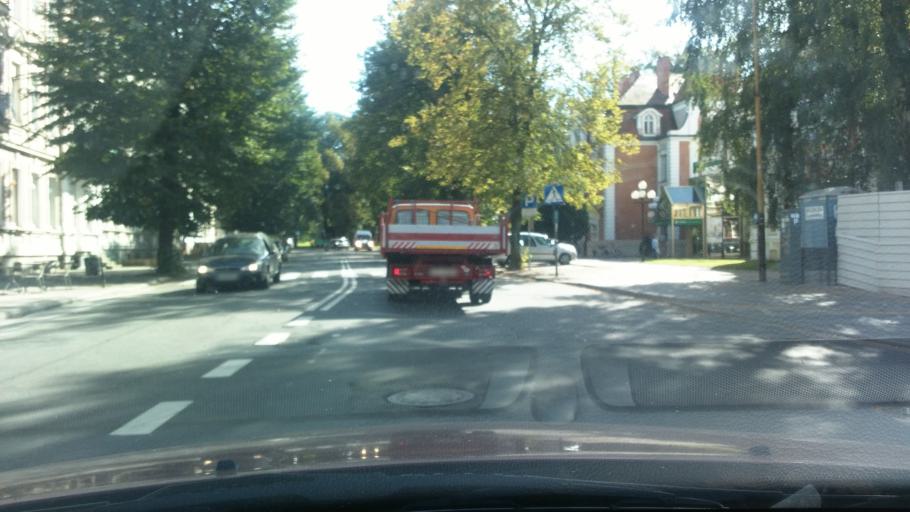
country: PL
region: Lower Silesian Voivodeship
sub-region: Powiat zgorzelecki
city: Zgorzelec
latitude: 51.1499
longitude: 15.0028
